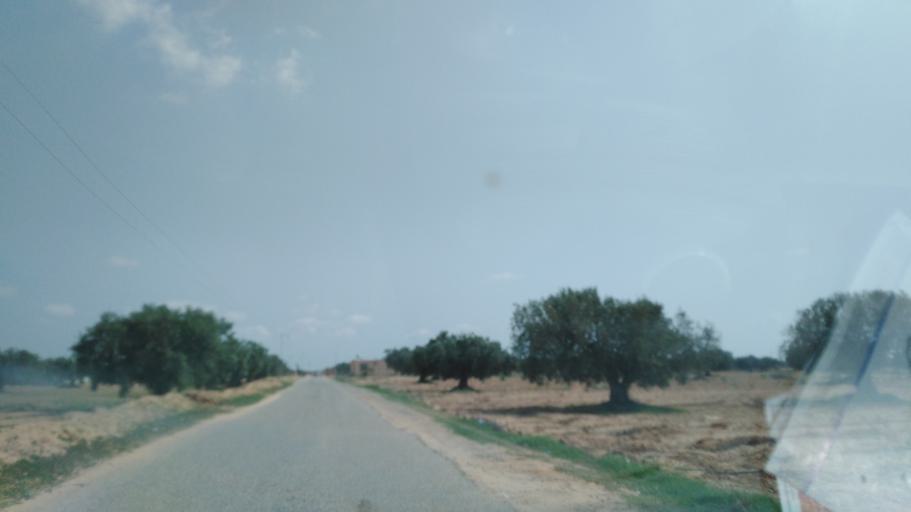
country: TN
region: Safaqis
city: Sfax
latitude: 34.6368
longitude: 10.6106
